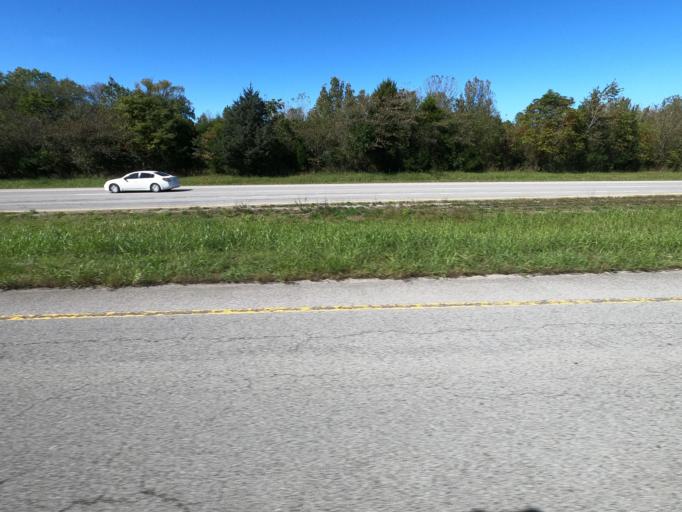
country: US
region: Tennessee
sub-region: Maury County
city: Mount Pleasant
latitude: 35.5086
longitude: -87.2257
